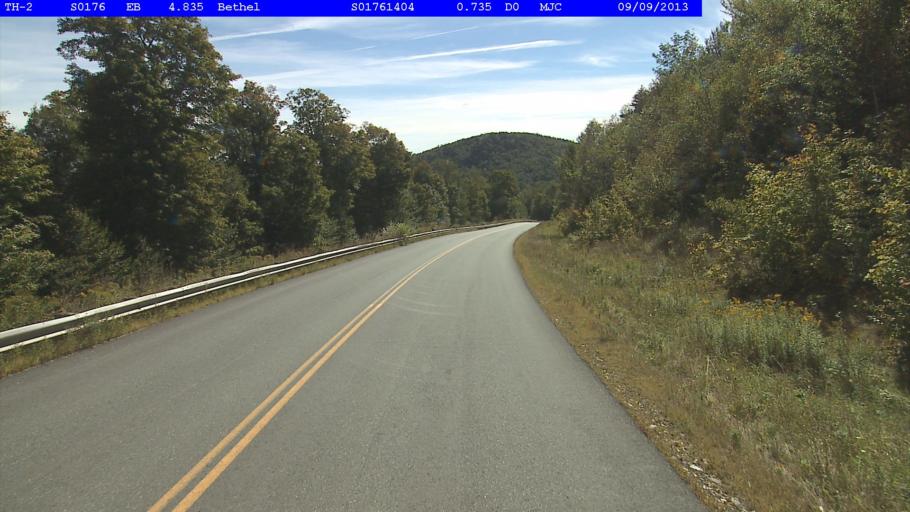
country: US
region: Vermont
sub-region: Orange County
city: Randolph
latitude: 43.8508
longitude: -72.7367
